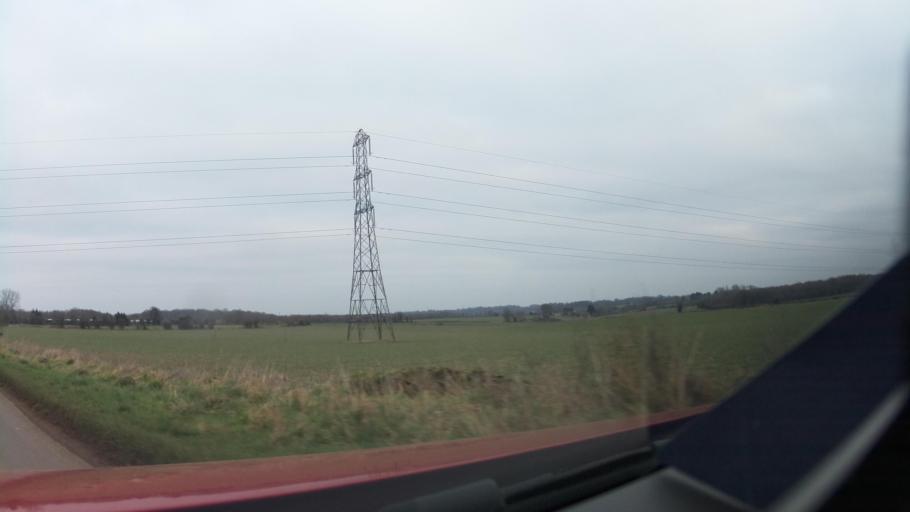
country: GB
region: England
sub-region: Wiltshire
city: Nettleton
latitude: 51.4870
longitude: -2.2813
